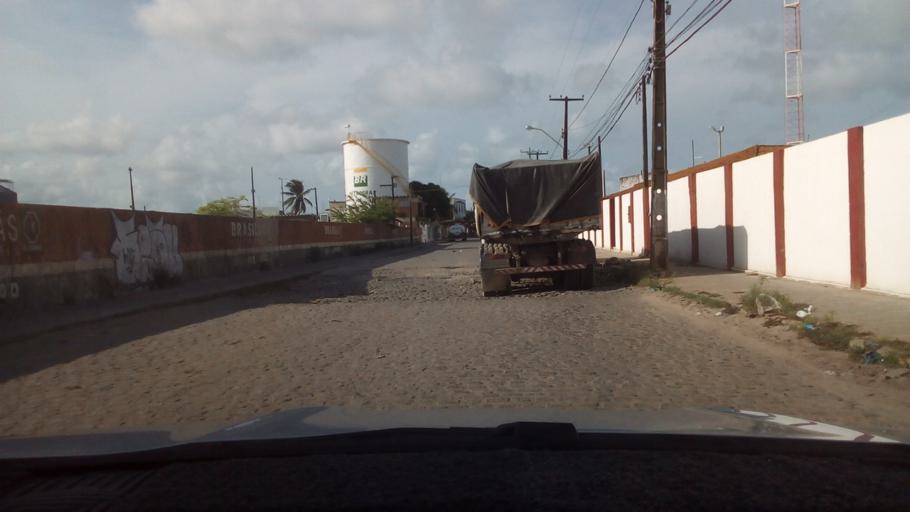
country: BR
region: Paraiba
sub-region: Cabedelo
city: Cabedelo
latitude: -6.9679
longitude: -34.8379
